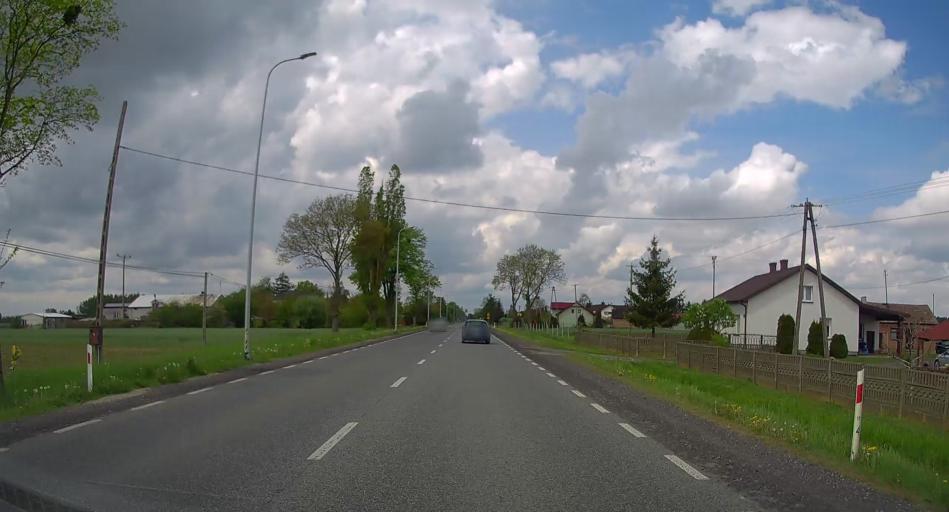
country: PL
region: Masovian Voivodeship
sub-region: Powiat plonski
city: Zaluski
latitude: 52.4451
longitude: 20.5178
